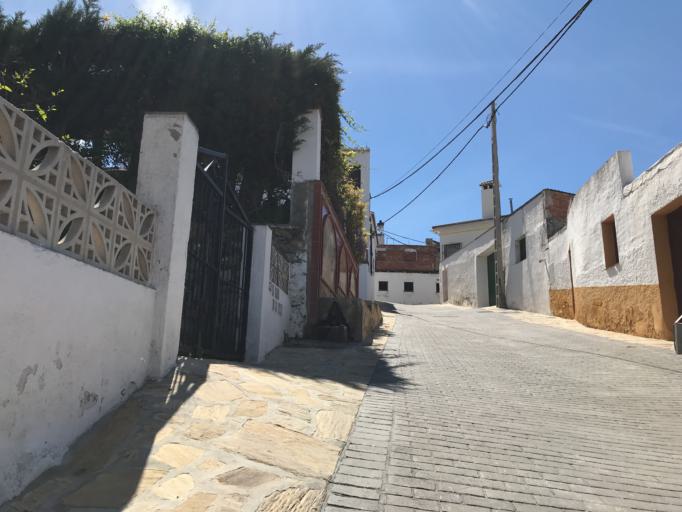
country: ES
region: Andalusia
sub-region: Provincia de Malaga
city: Alcaucin
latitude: 36.9035
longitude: -4.1154
